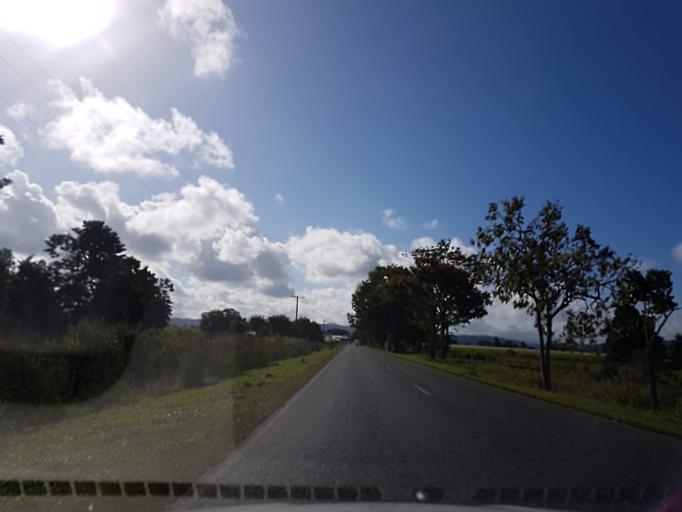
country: AU
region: Queensland
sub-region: Cairns
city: Port Douglas
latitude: -16.4078
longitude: 145.3830
